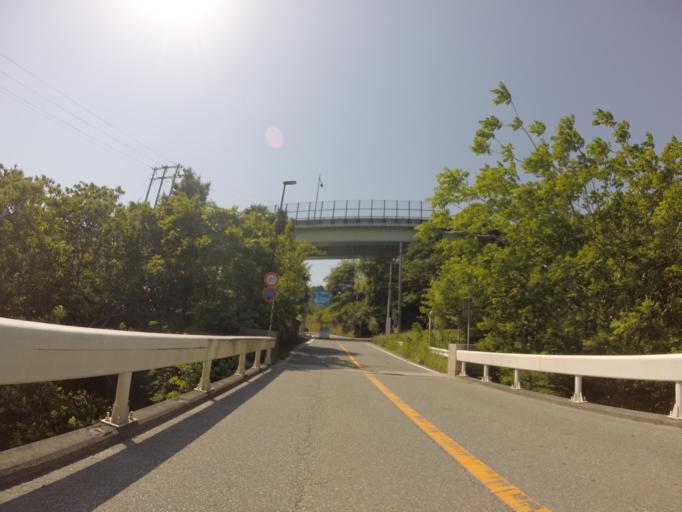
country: JP
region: Shizuoka
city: Fujinomiya
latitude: 35.1926
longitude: 138.5695
